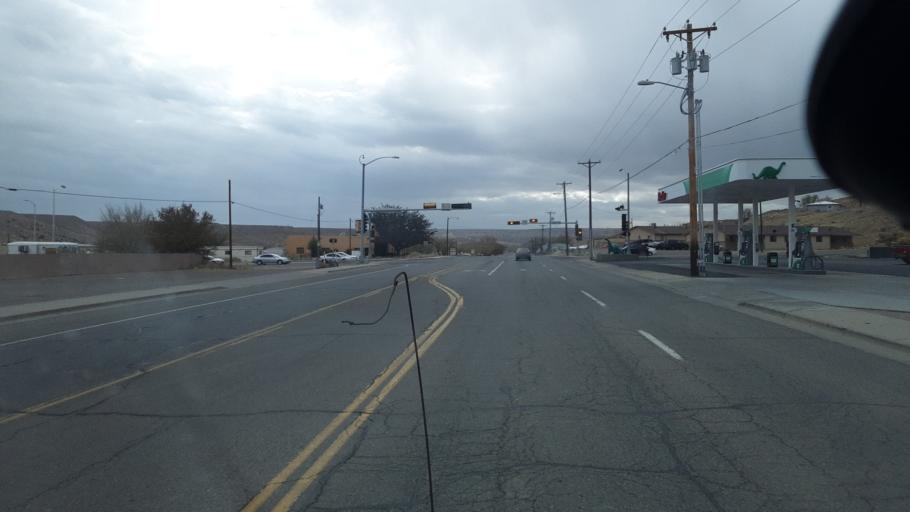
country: US
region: New Mexico
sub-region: San Juan County
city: Farmington
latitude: 36.7590
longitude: -108.2419
